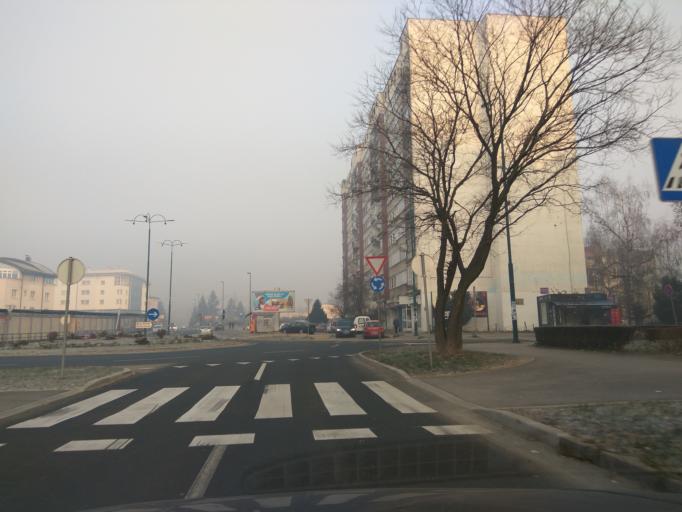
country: BA
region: Federation of Bosnia and Herzegovina
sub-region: Kanton Sarajevo
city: Sarajevo
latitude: 43.8505
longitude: 18.3666
